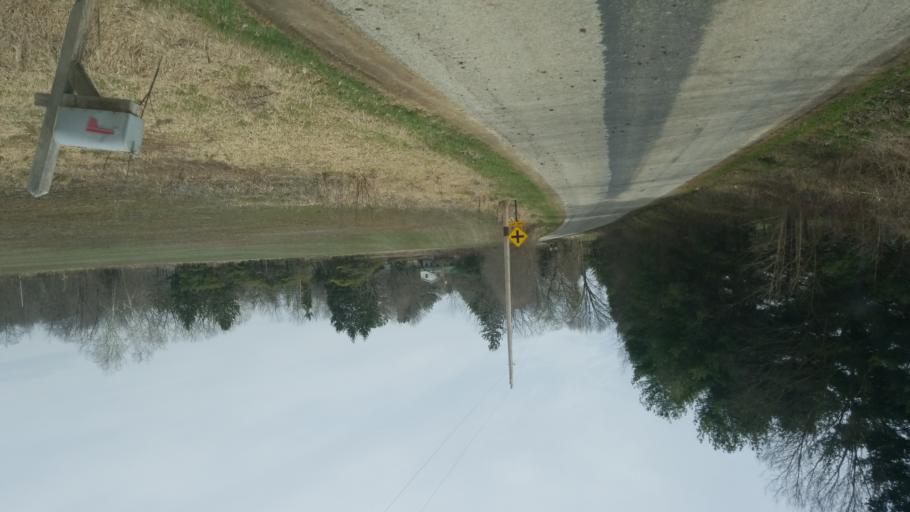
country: US
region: Ohio
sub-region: Licking County
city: Utica
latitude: 40.2466
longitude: -82.5756
